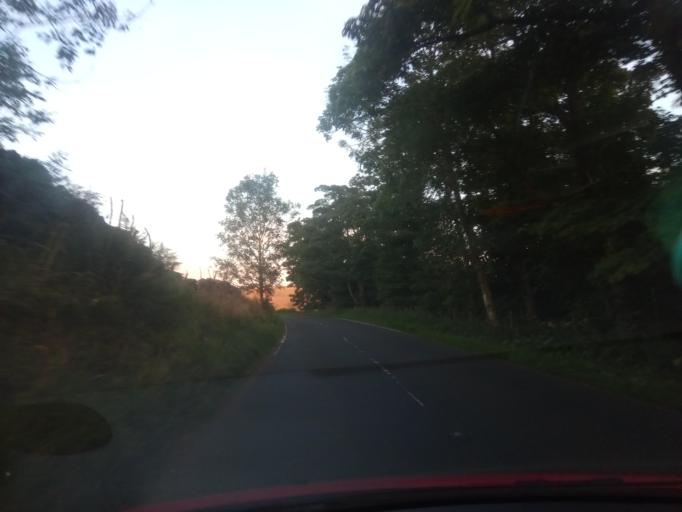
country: GB
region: England
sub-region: Northumberland
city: Bardon Mill
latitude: 54.8650
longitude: -2.3659
